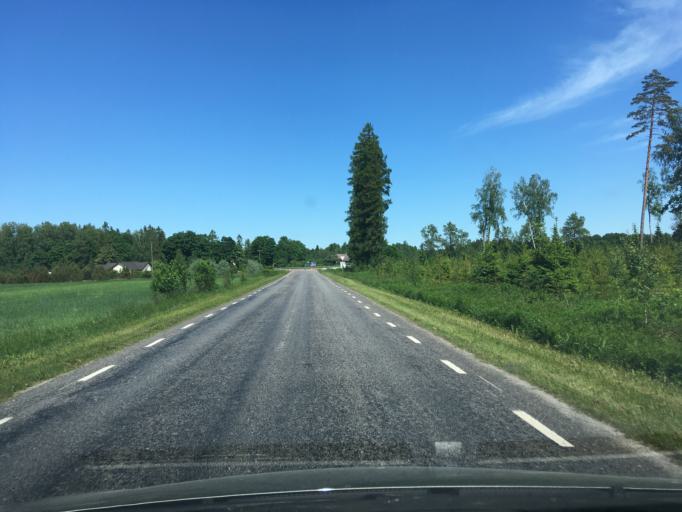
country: EE
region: Raplamaa
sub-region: Rapla vald
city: Rapla
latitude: 59.0662
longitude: 24.9134
